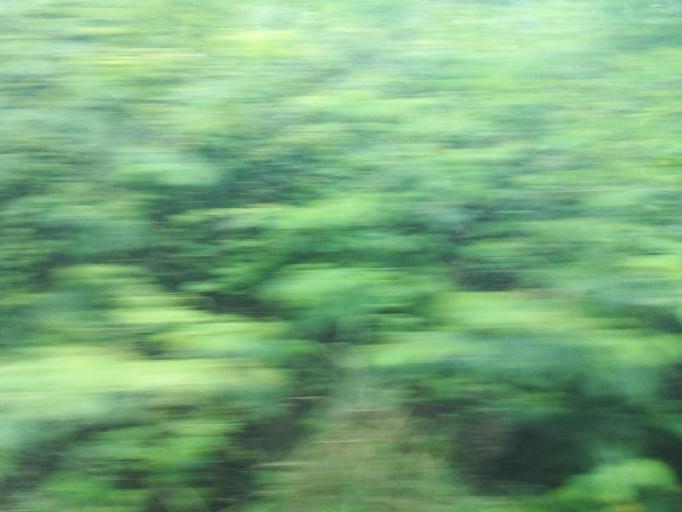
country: BR
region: Minas Gerais
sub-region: Joao Monlevade
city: Joao Monlevade
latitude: -19.8252
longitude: -43.1038
